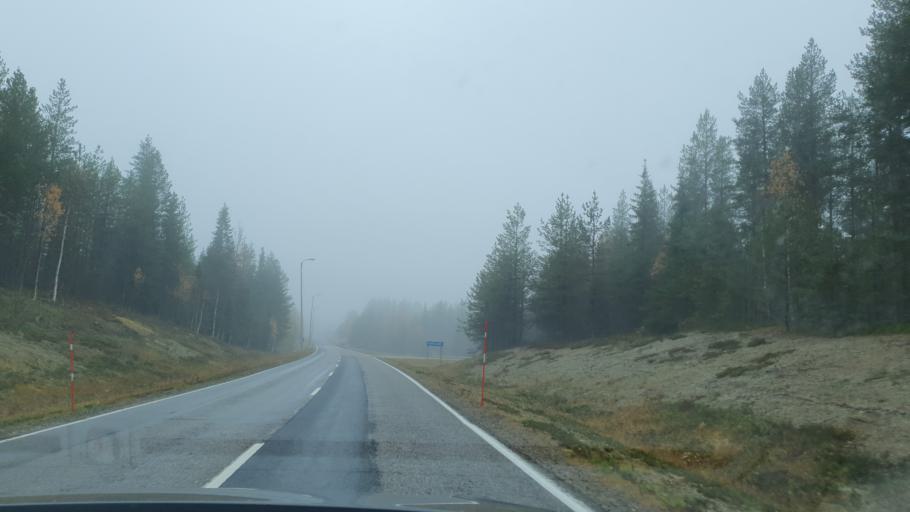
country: FI
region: Lapland
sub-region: Tunturi-Lappi
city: Kittilae
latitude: 67.2778
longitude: 24.8835
